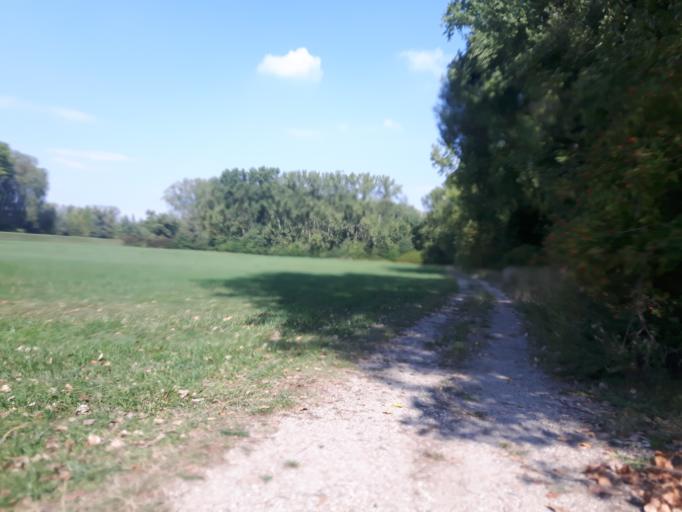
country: DE
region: Baden-Wuerttemberg
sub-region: Karlsruhe Region
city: Bruhl
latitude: 49.3943
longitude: 8.4970
